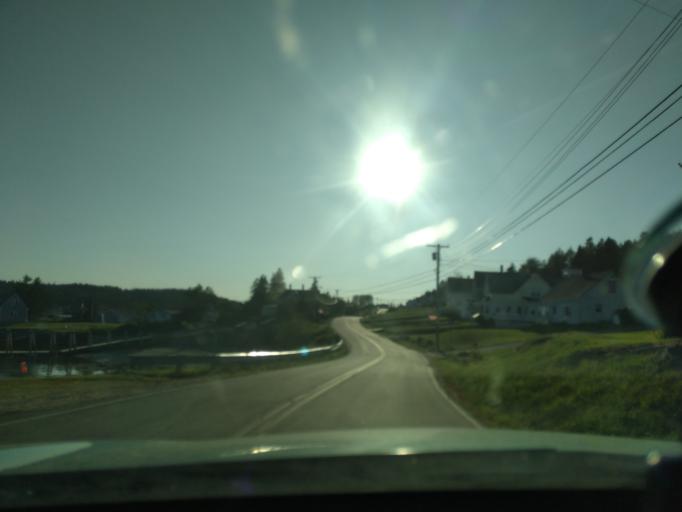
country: US
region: Maine
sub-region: Washington County
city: Machiasport
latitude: 44.6577
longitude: -67.2057
